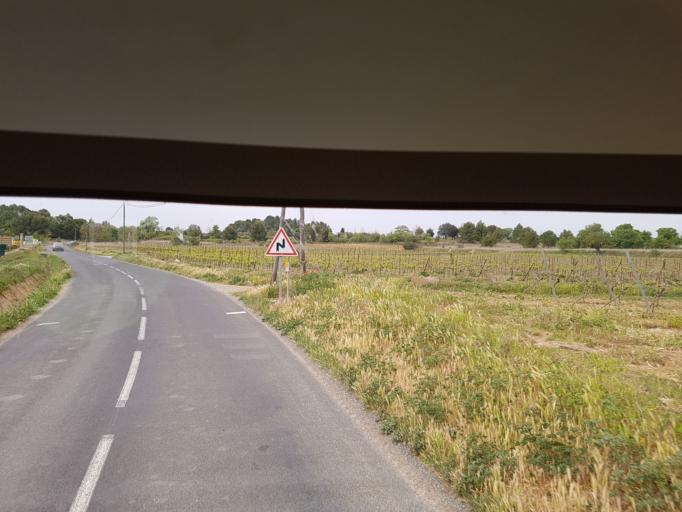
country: FR
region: Languedoc-Roussillon
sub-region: Departement de l'Aude
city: Fleury
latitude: 43.2202
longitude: 3.1333
